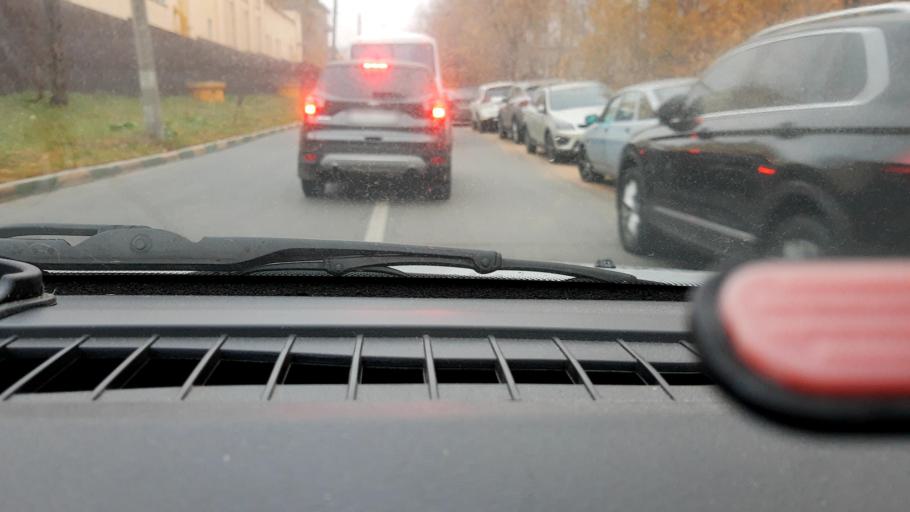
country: RU
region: Nizjnij Novgorod
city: Nizhniy Novgorod
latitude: 56.2506
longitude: 43.9746
